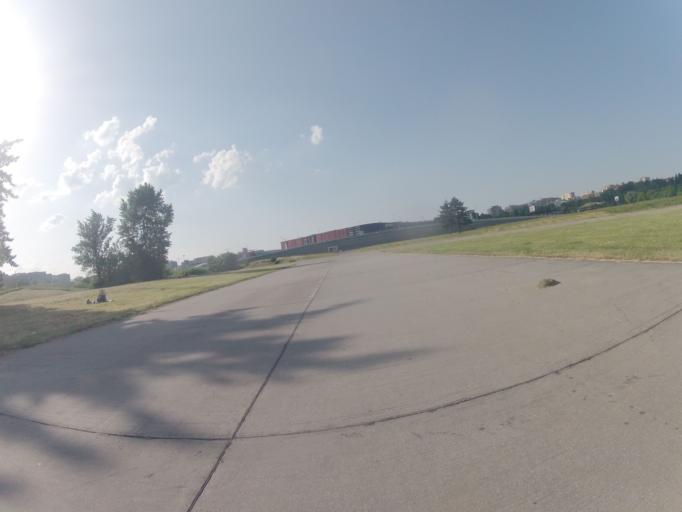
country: PL
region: Lesser Poland Voivodeship
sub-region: Krakow
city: Krakow
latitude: 50.0837
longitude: 19.9878
